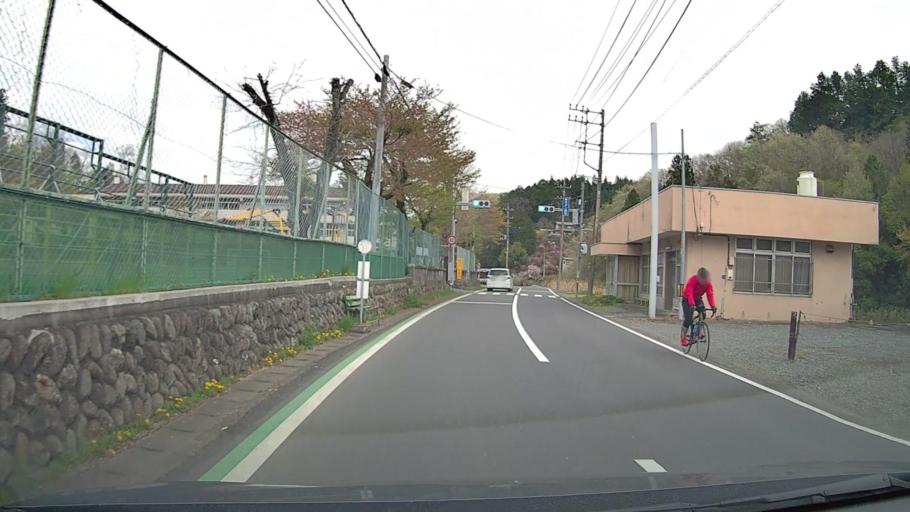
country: JP
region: Saitama
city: Chichibu
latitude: 36.0553
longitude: 139.1309
